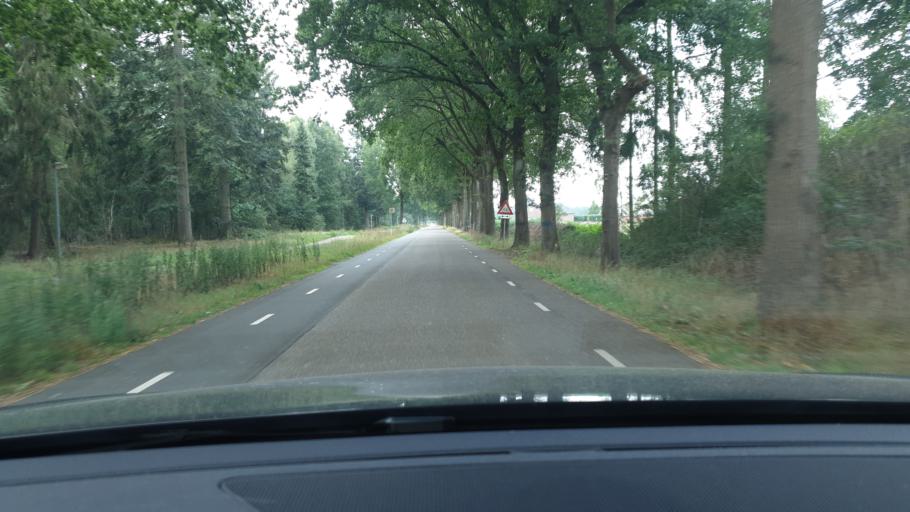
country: NL
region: North Brabant
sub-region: Gemeente Veldhoven
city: Oerle
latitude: 51.4434
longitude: 5.3190
